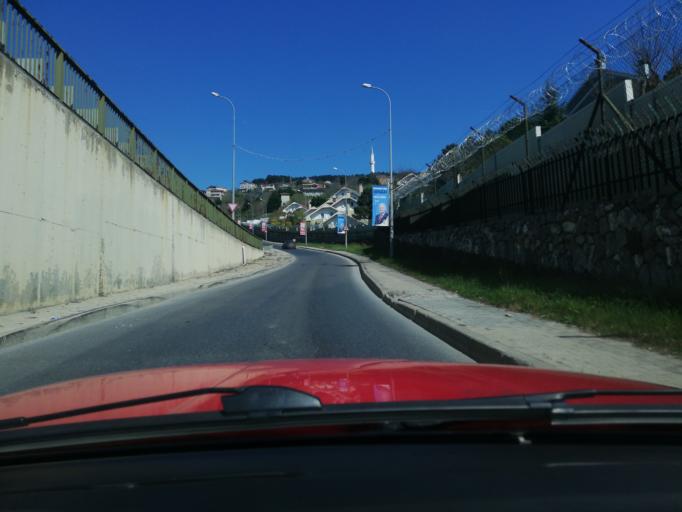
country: TR
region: Istanbul
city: Mahmut Sevket Pasa
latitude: 41.1215
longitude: 29.1304
